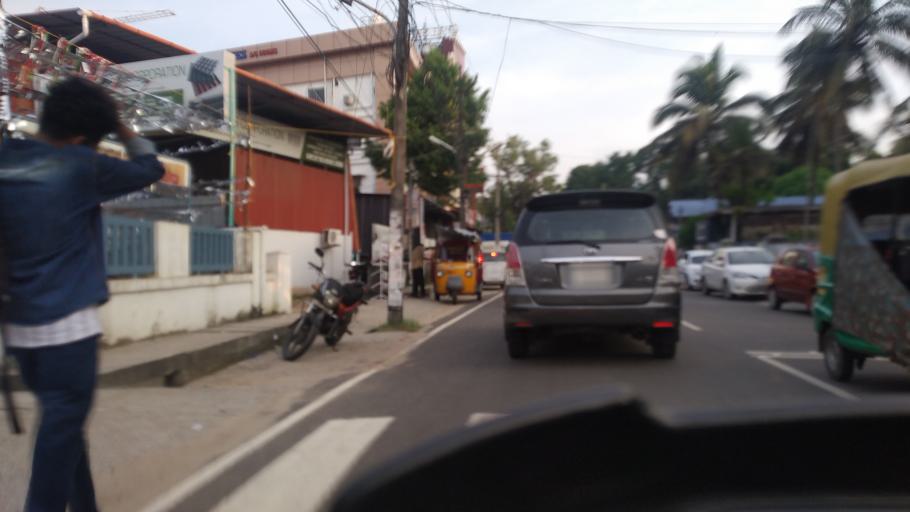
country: IN
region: Kerala
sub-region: Ernakulam
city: Elur
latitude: 10.0311
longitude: 76.3039
